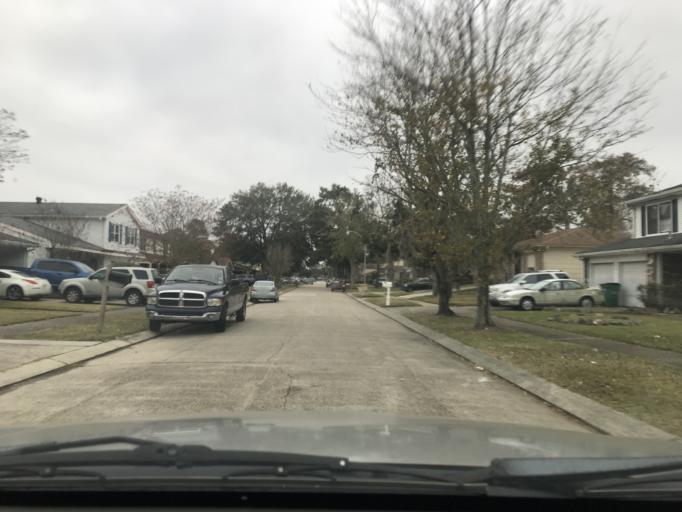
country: US
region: Louisiana
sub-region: Jefferson Parish
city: Woodmere
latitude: 29.8669
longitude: -90.0803
